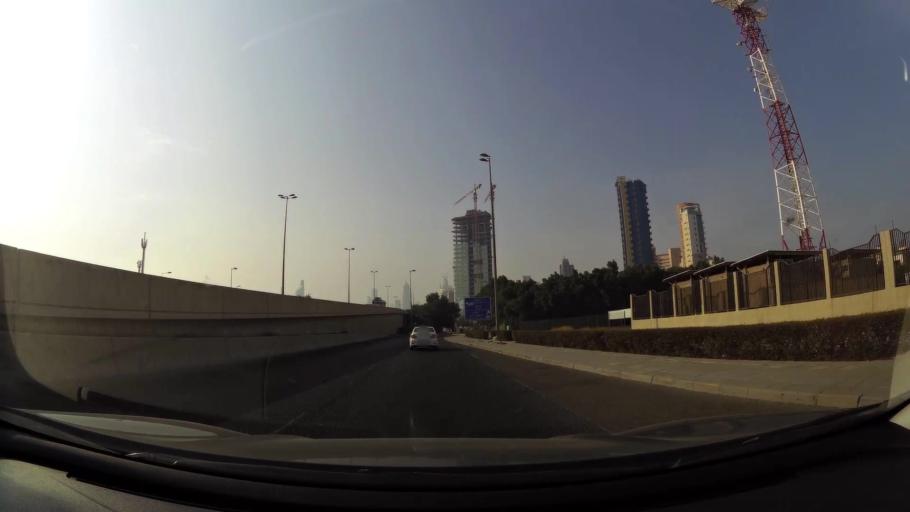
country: KW
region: Al Asimah
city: Ad Dasmah
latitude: 29.3650
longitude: 48.0127
